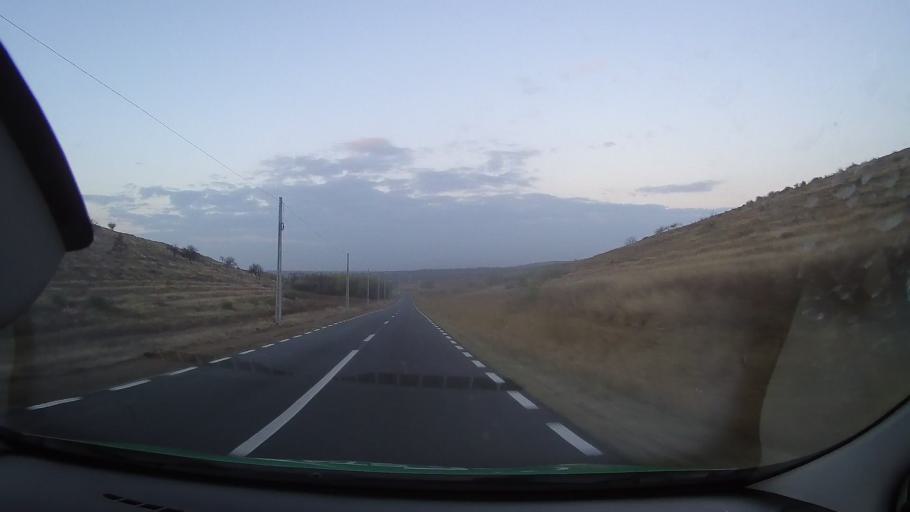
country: RO
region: Constanta
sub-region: Comuna Oltina
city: Oltina
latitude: 44.1464
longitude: 27.6667
